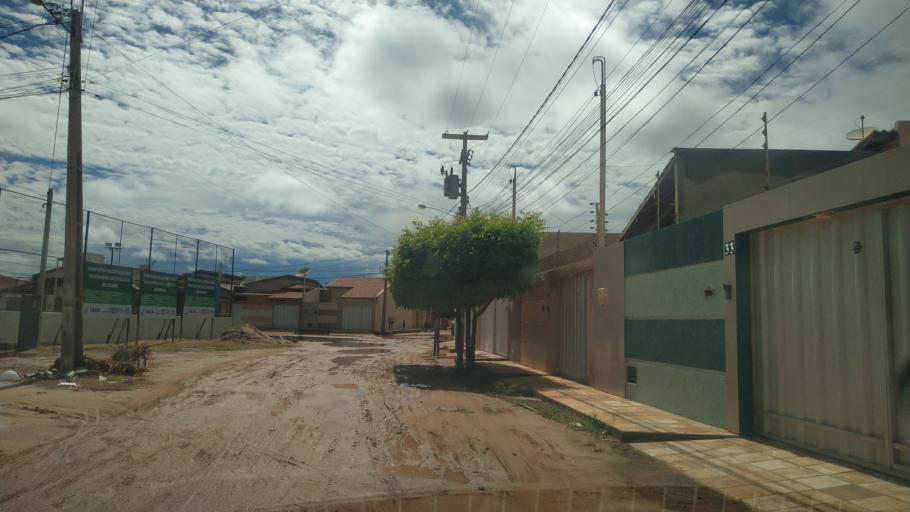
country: BR
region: Rio Grande do Norte
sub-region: Areia Branca
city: Areia Branca
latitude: -4.9539
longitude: -37.1228
